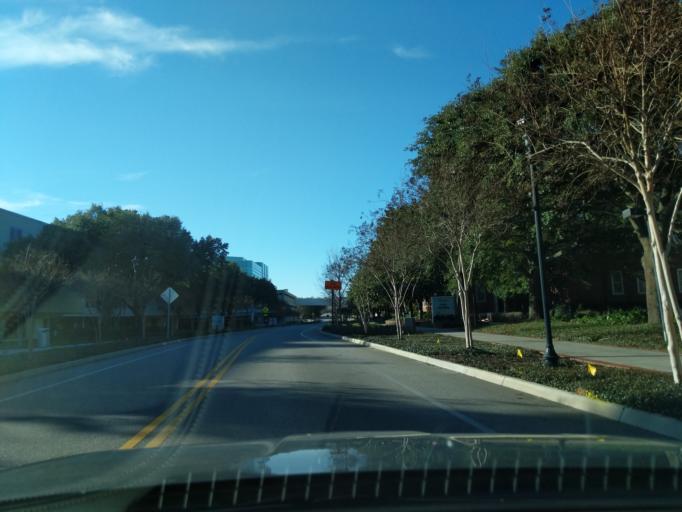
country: US
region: Georgia
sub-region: Richmond County
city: Augusta
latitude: 33.4688
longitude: -81.9878
